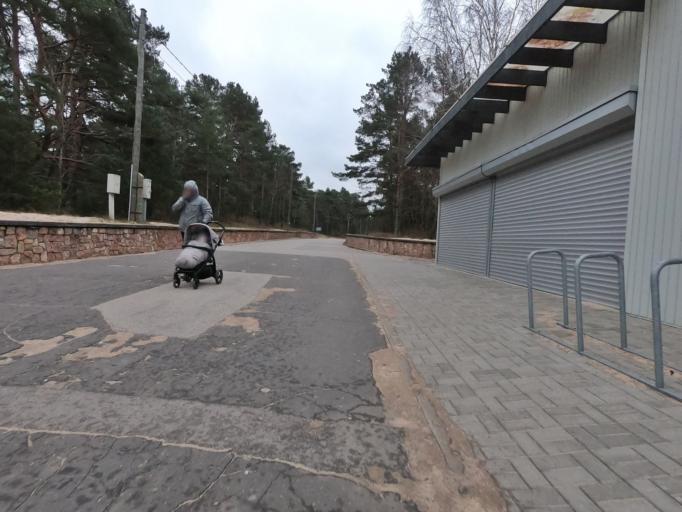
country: LV
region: Riga
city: Bolderaja
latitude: 57.0811
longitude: 24.1079
